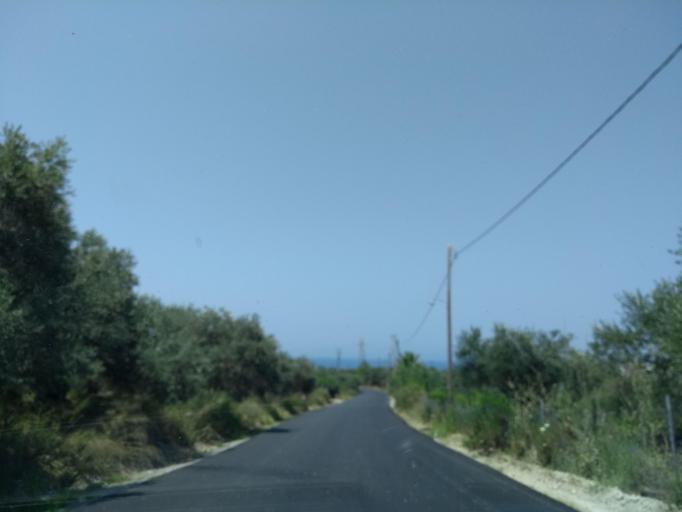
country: GR
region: Crete
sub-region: Nomos Chanias
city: Georgioupolis
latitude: 35.3357
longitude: 24.3019
